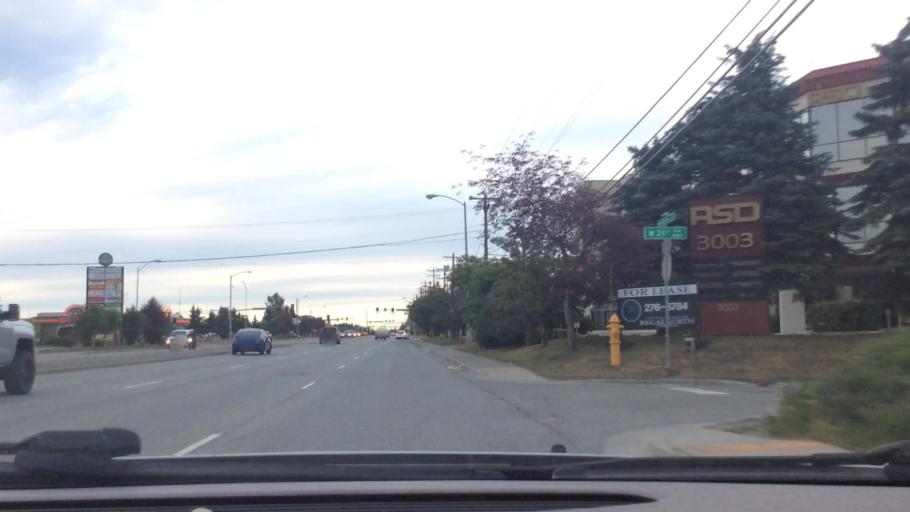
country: US
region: Alaska
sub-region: Anchorage Municipality
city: Anchorage
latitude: 61.1919
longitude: -149.9128
